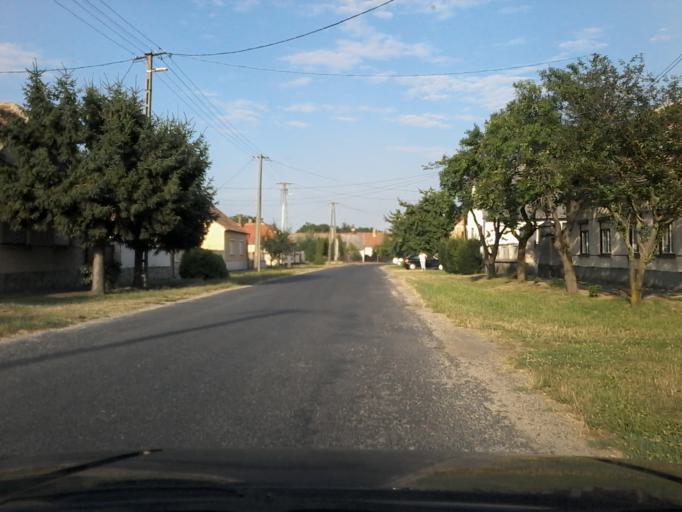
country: HU
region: Vas
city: Janoshaza
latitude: 47.0934
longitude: 17.1909
